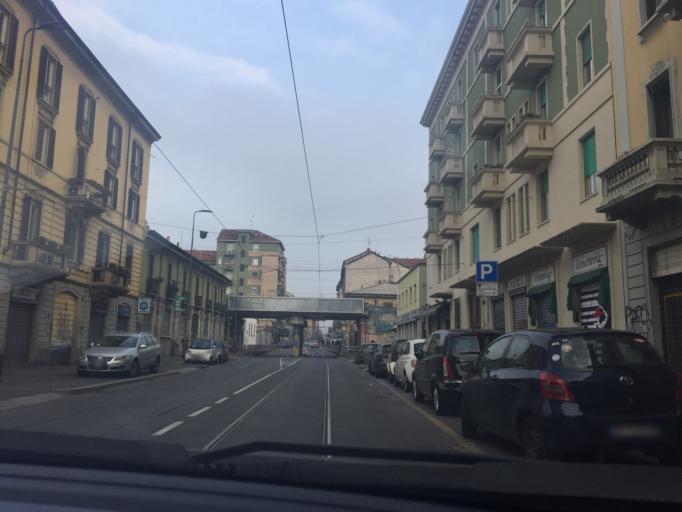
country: IT
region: Lombardy
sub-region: Citta metropolitana di Milano
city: Milano
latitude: 45.4419
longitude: 9.1788
